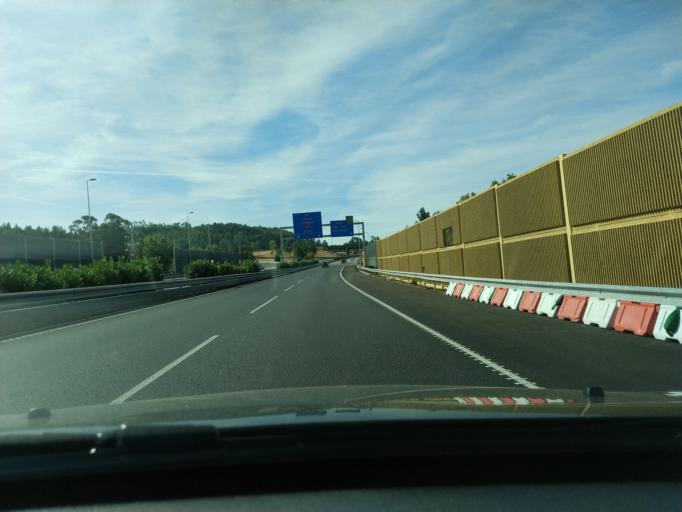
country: PT
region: Aveiro
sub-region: Mealhada
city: Pampilhosa do Botao
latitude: 40.2776
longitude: -8.4785
